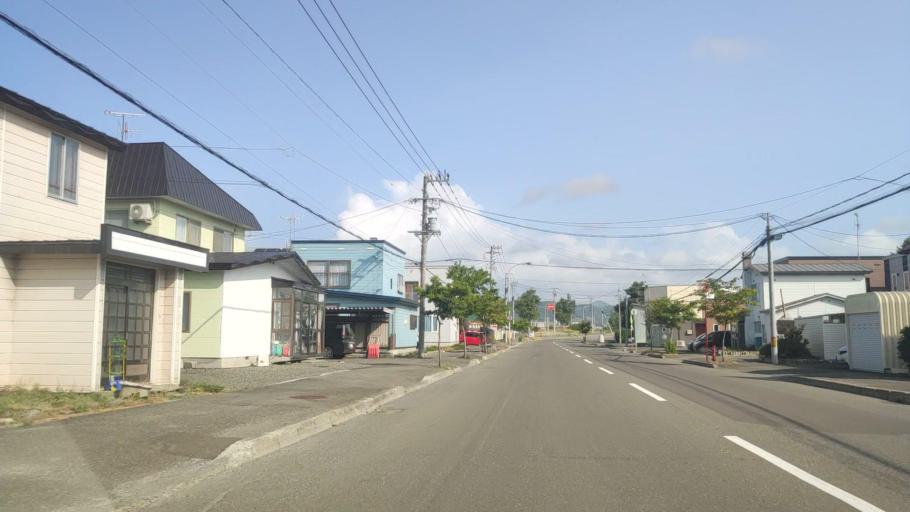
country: JP
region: Hokkaido
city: Shimo-furano
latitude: 43.3522
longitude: 142.3909
